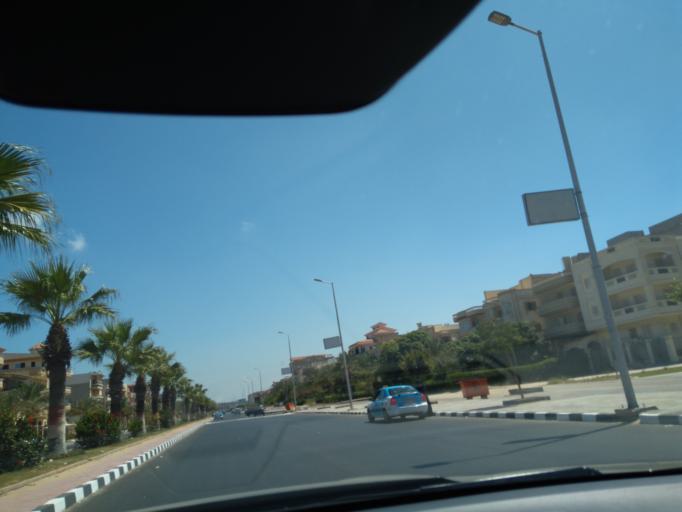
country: EG
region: Dumyat
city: Faraskur
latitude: 31.4320
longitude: 31.6732
